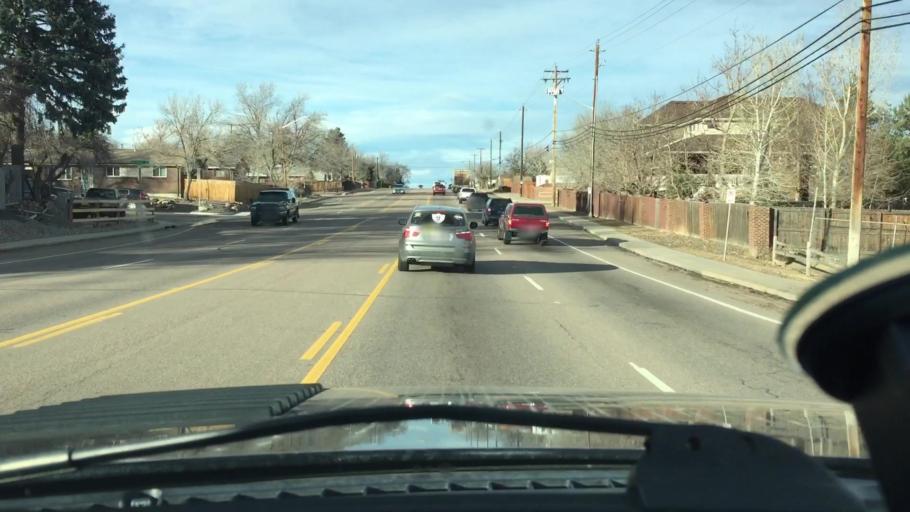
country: US
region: Colorado
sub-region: Adams County
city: Sherrelwood
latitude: 39.8430
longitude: -105.0060
